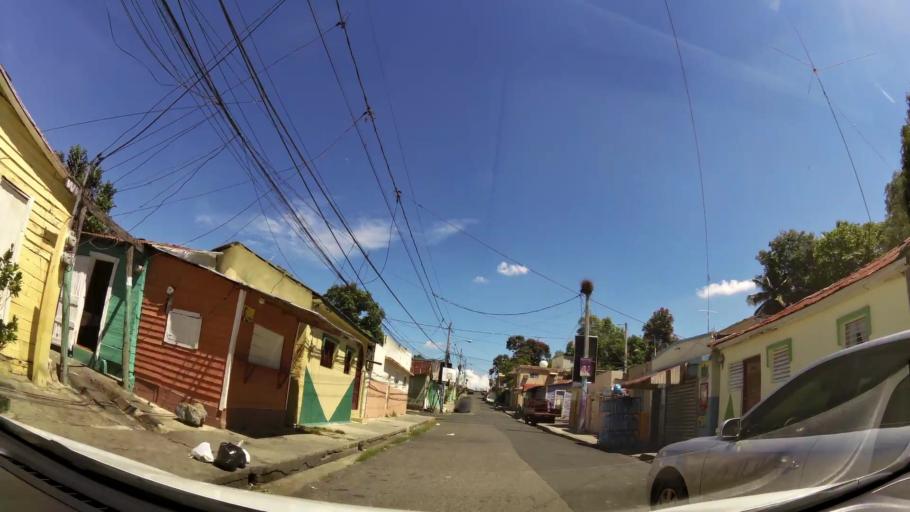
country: DO
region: Santiago
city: Santiago de los Caballeros
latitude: 19.4469
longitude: -70.6990
